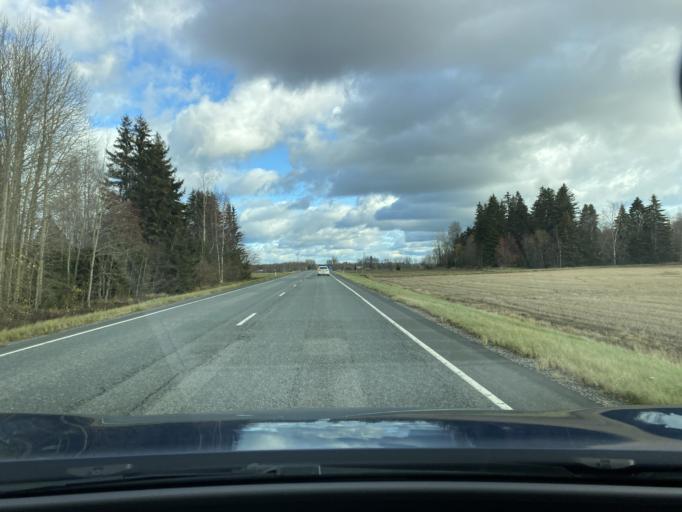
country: FI
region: Haeme
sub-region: Forssa
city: Humppila
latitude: 60.9497
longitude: 23.3233
